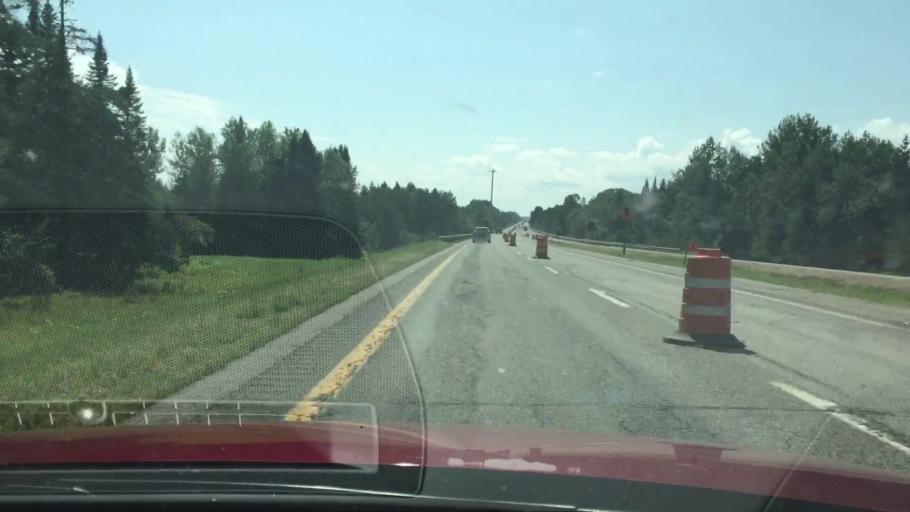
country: US
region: Maine
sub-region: Penobscot County
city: Patten
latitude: 45.8721
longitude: -68.4138
